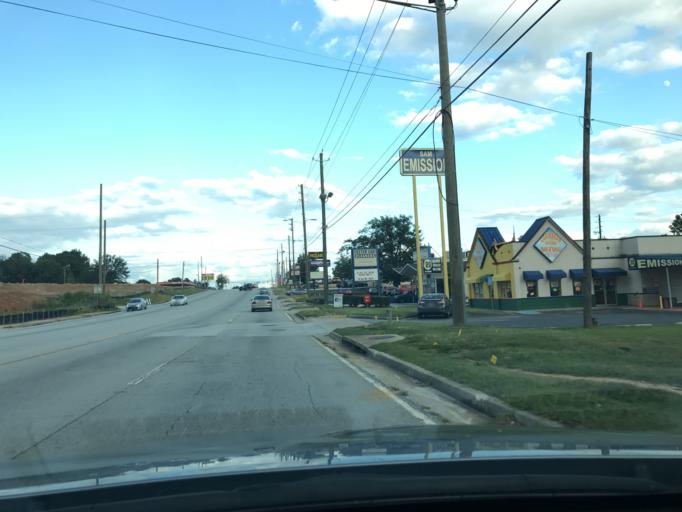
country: US
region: Georgia
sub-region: Douglas County
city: Douglasville
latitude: 33.7511
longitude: -84.7302
